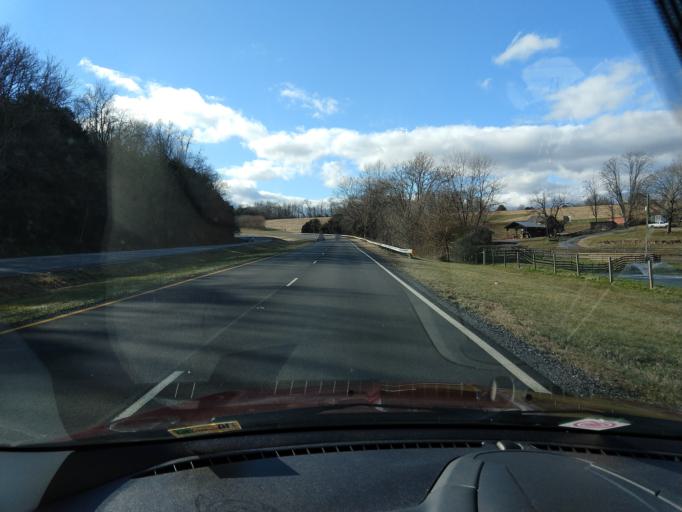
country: US
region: Virginia
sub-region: Rockbridge County
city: East Lexington
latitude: 37.7553
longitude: -79.4015
